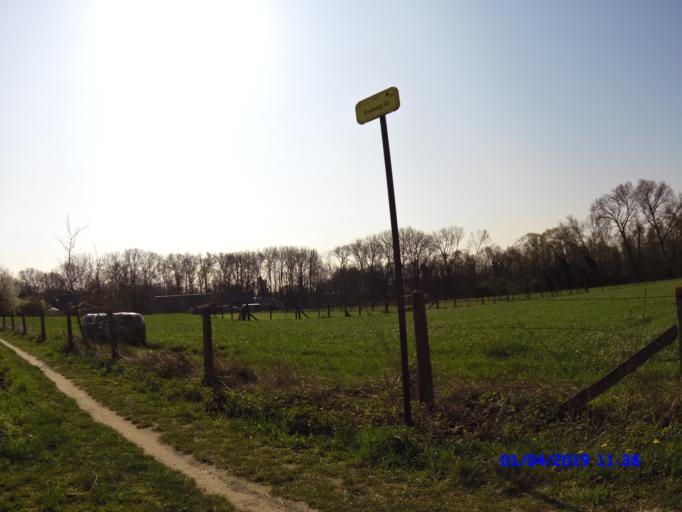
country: BE
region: Flanders
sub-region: Provincie Vlaams-Brabant
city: Ternat
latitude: 50.8739
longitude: 4.1916
